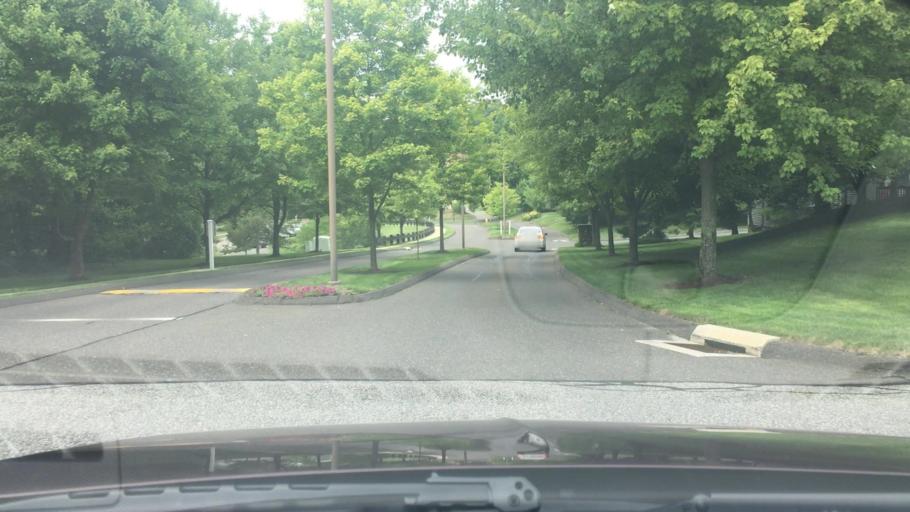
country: US
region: Connecticut
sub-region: Fairfield County
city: Danbury
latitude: 41.4339
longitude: -73.4231
